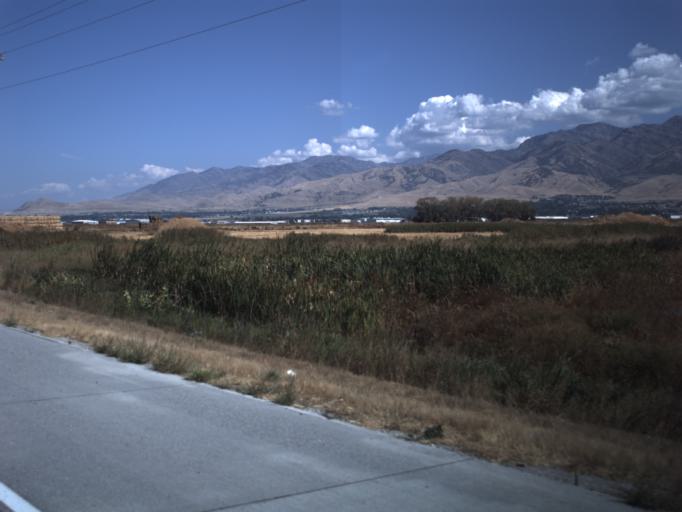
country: US
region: Utah
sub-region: Cache County
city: Logan
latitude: 41.7688
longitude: -111.8585
